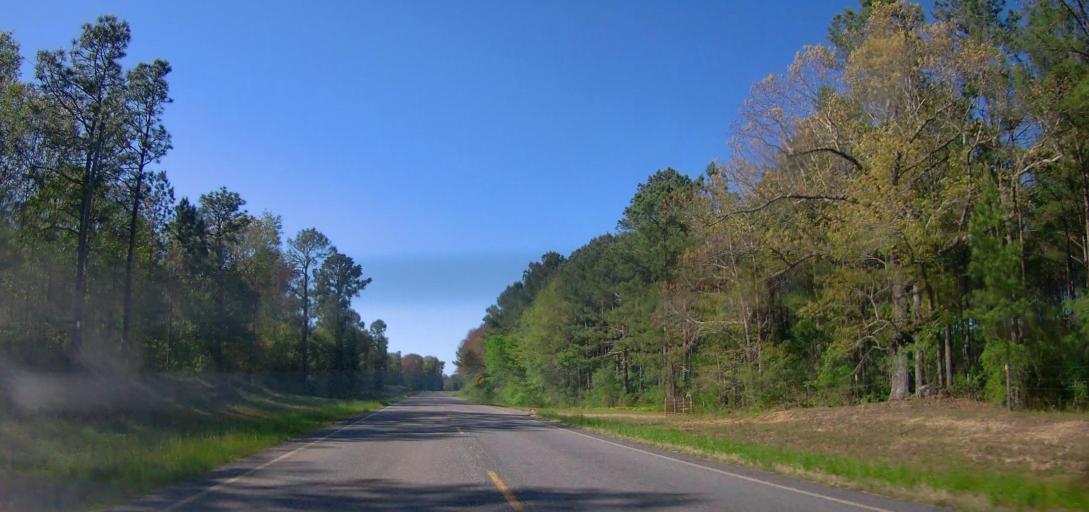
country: US
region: Georgia
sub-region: Wilcox County
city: Rochelle
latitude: 32.0278
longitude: -83.5020
